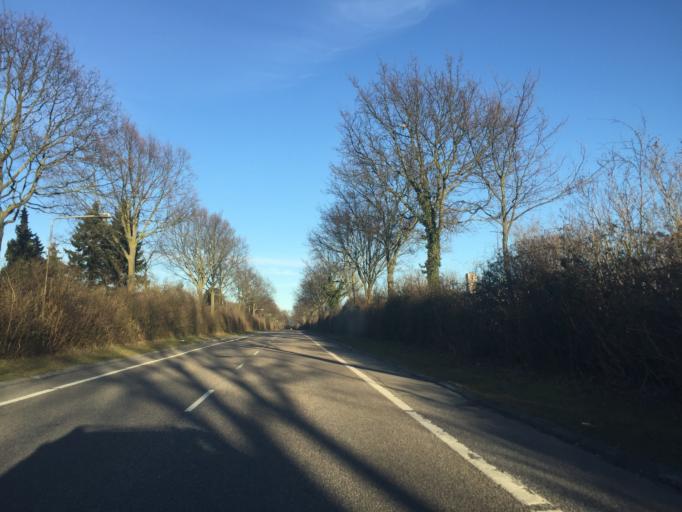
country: DK
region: Capital Region
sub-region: Dragor Kommune
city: Dragor
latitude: 55.5896
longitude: 12.6463
